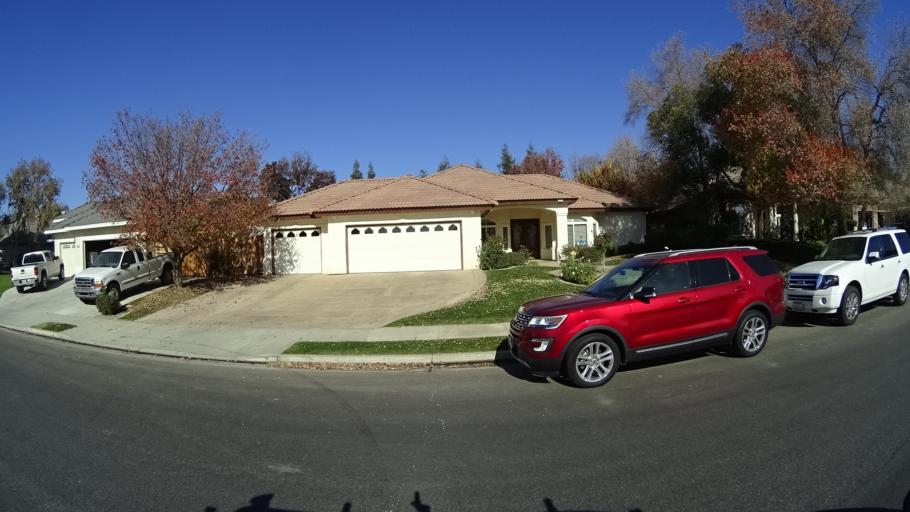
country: US
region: California
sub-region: Kern County
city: Rosedale
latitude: 35.3660
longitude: -119.1421
